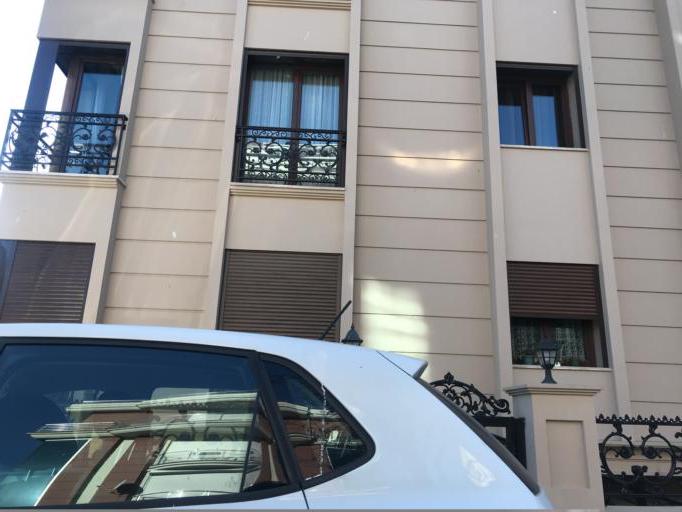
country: TR
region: Istanbul
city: Bahcelievler
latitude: 40.9598
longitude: 28.8335
